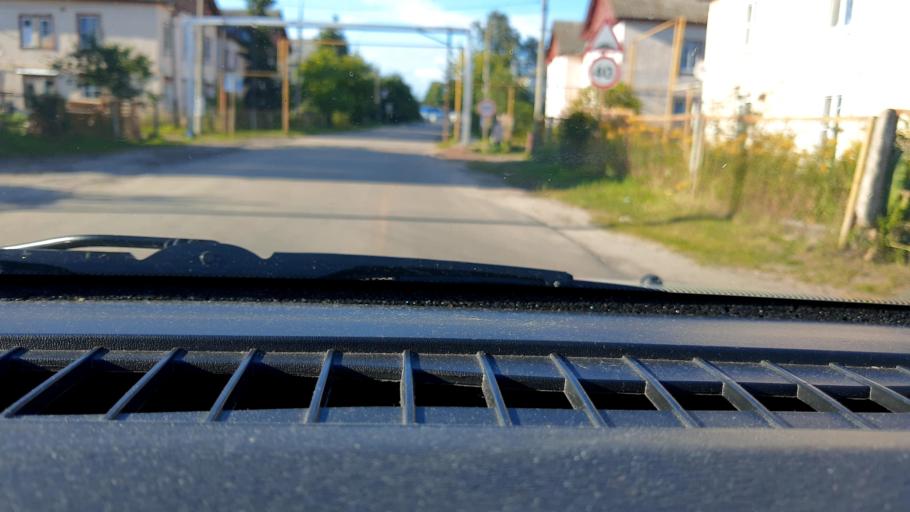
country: RU
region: Nizjnij Novgorod
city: Lukino
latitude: 56.3359
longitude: 43.6177
